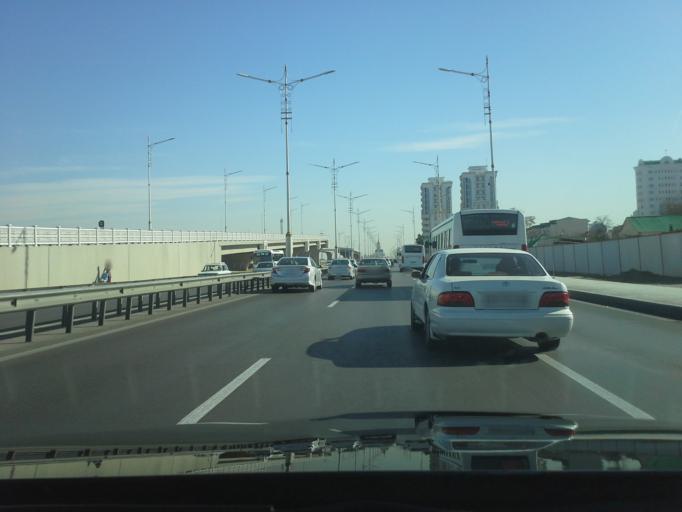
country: TM
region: Ahal
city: Ashgabat
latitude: 37.9492
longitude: 58.3840
